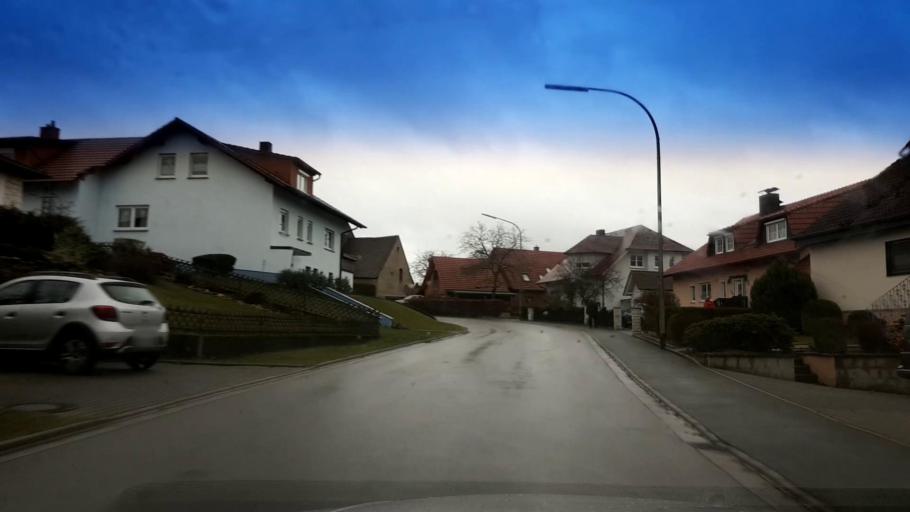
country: DE
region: Bavaria
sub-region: Upper Franconia
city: Litzendorf
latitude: 49.8725
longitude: 11.0447
